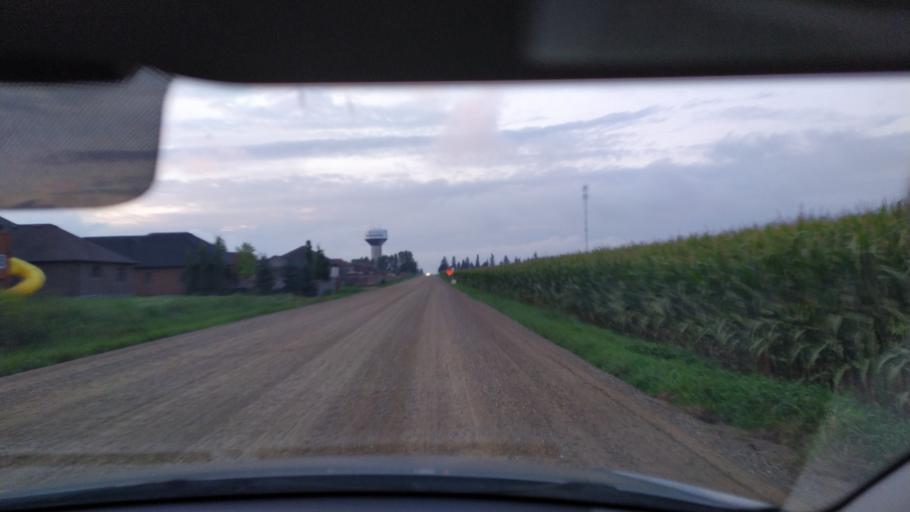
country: CA
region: Ontario
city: Kitchener
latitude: 43.3074
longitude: -80.6102
